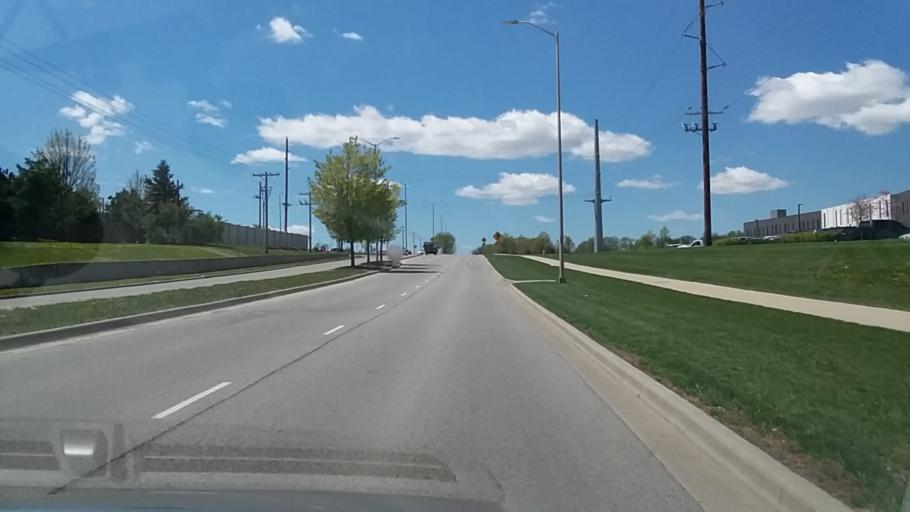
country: US
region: Kansas
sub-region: Johnson County
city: Olathe
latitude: 38.8839
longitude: -94.8513
